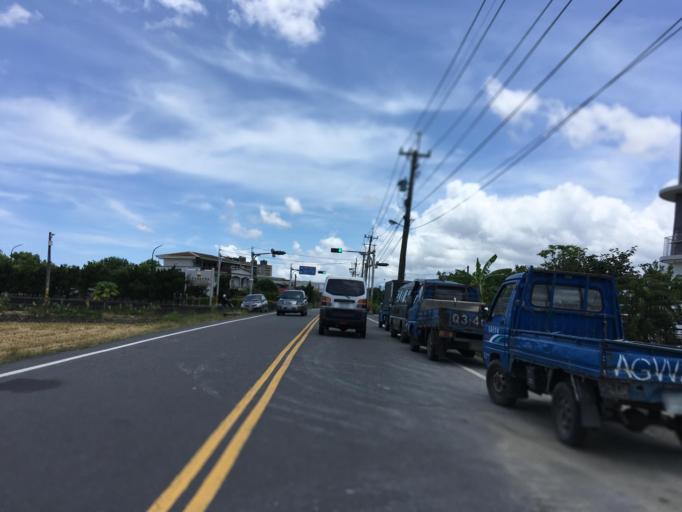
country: TW
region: Taiwan
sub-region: Yilan
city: Yilan
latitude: 24.6960
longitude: 121.7654
